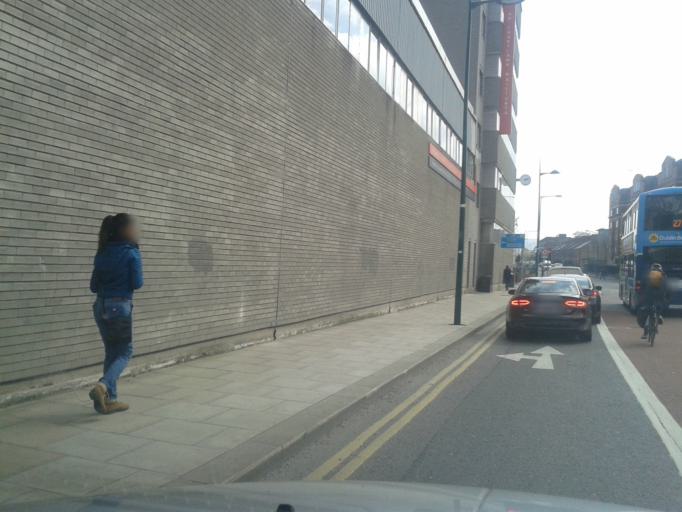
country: IE
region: Leinster
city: Rathmines
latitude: 53.3389
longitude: -6.2693
